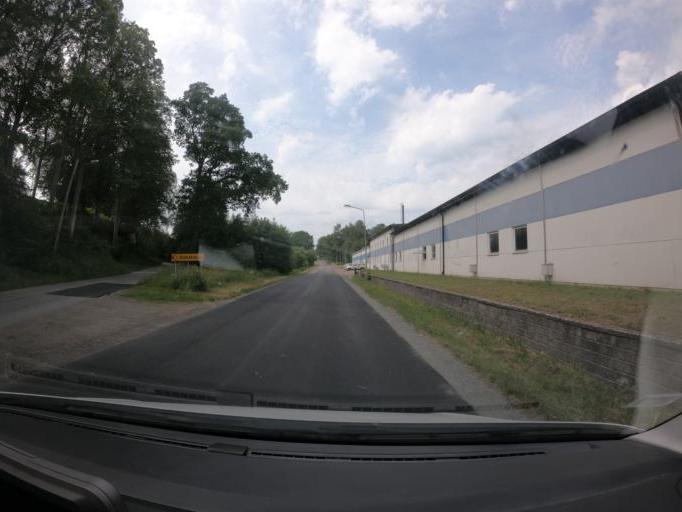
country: SE
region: Skane
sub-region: Hassleholms Kommun
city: Bjarnum
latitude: 56.2889
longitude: 13.7070
